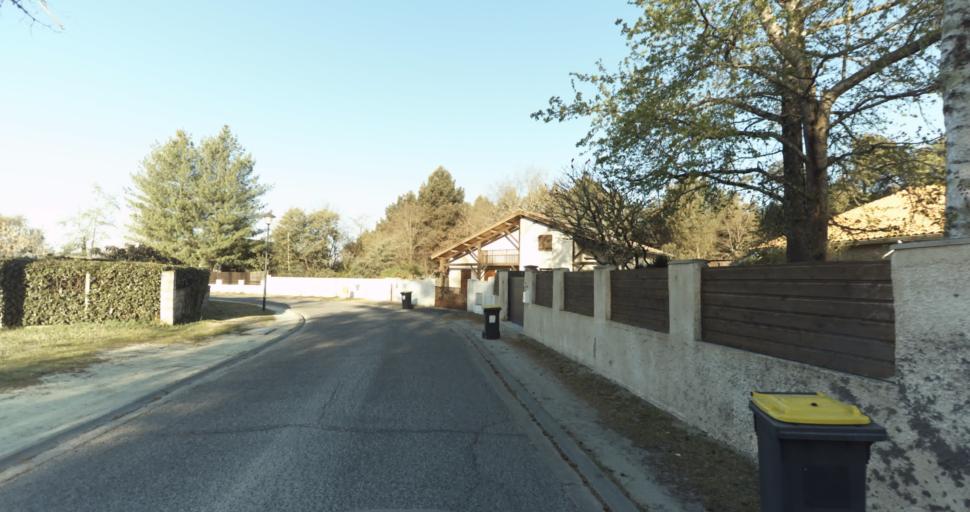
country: FR
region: Aquitaine
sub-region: Departement de la Gironde
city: Martignas-sur-Jalle
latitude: 44.8157
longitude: -0.7850
